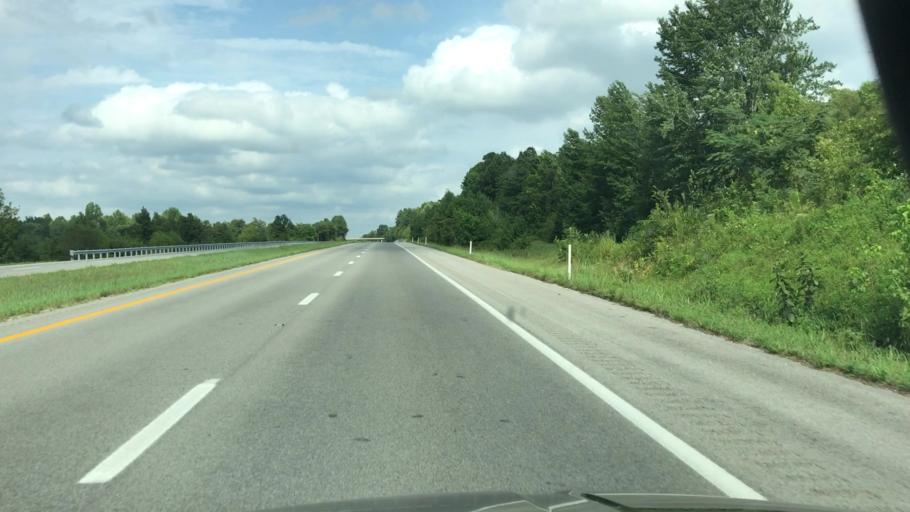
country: US
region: Kentucky
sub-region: Hopkins County
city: Dawson Springs
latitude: 37.1674
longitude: -87.7506
